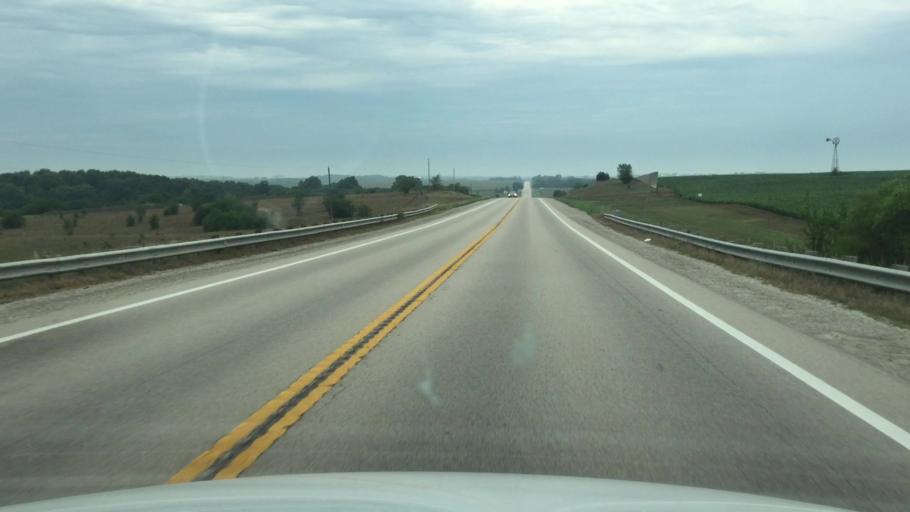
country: US
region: Kansas
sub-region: Brown County
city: Hiawatha
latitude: 39.8486
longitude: -95.6227
